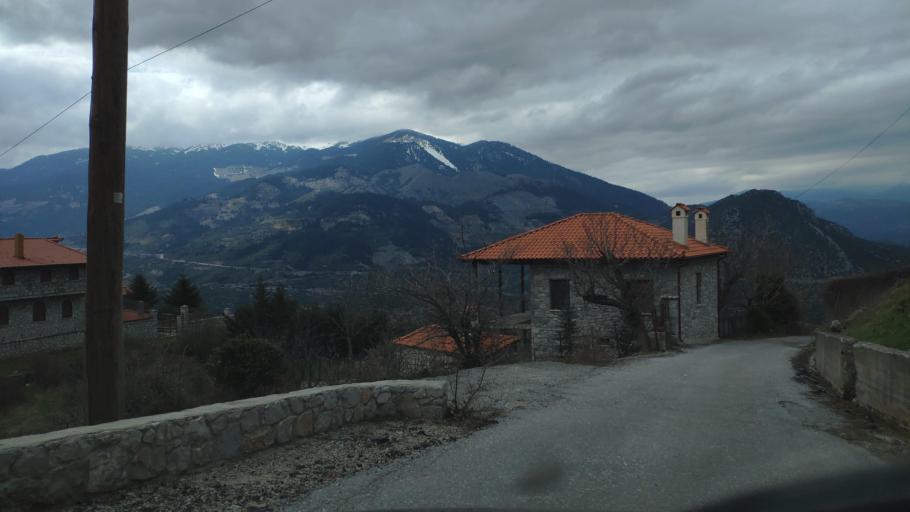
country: GR
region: Central Greece
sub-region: Nomos Fokidos
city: Amfissa
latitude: 38.6410
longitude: 22.4224
